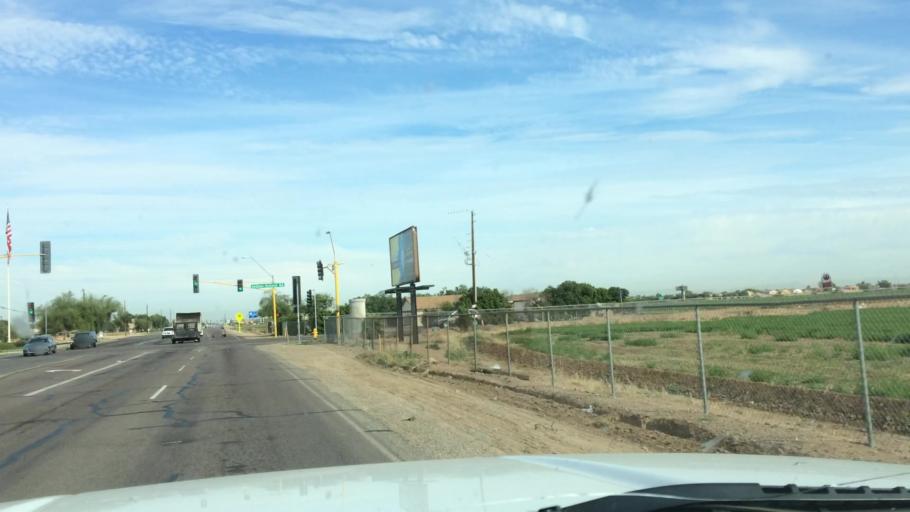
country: US
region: Arizona
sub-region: Maricopa County
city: Tolleson
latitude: 33.4931
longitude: -112.2724
